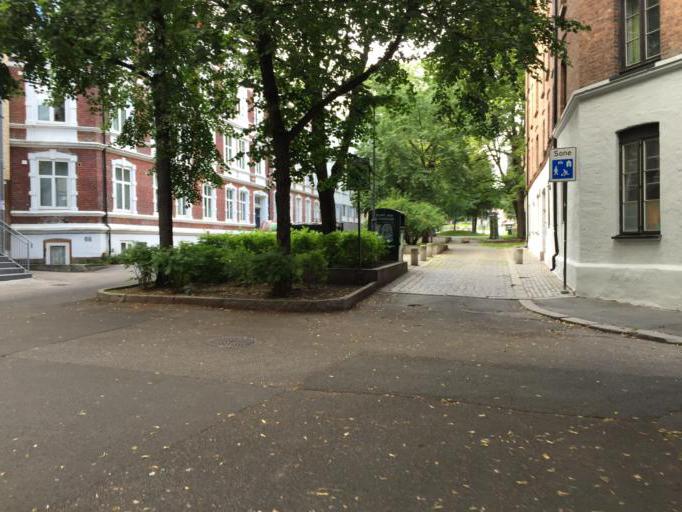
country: NO
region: Oslo
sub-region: Oslo
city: Oslo
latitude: 59.9190
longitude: 10.7657
